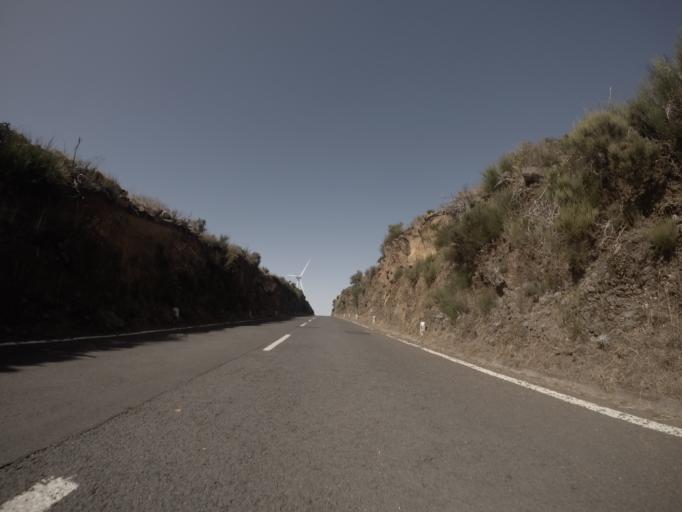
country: PT
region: Madeira
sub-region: Sao Vicente
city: Sao Vicente
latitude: 32.7450
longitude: -17.0572
